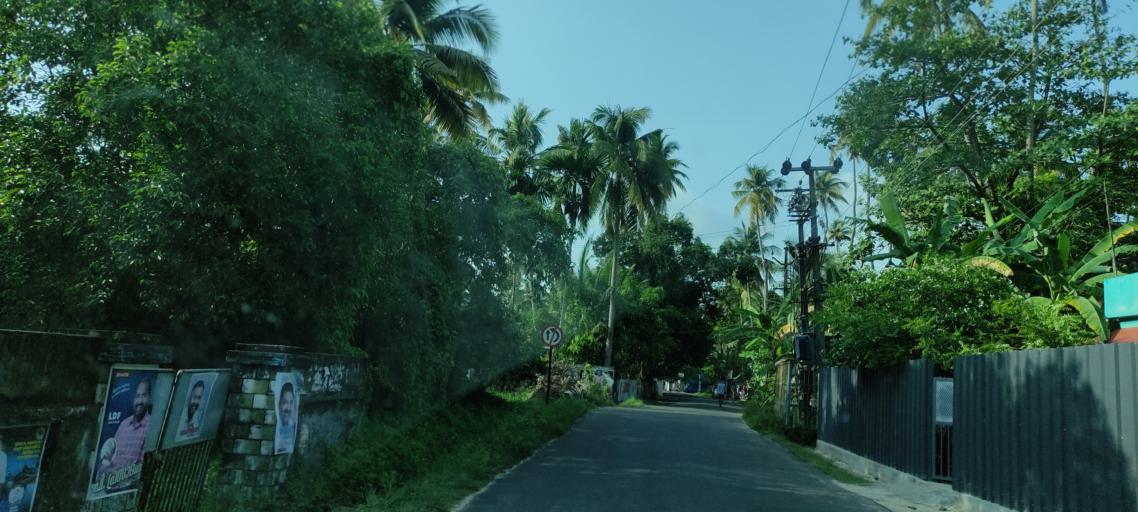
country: IN
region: Kerala
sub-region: Alappuzha
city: Vayalar
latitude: 9.7263
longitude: 76.2867
